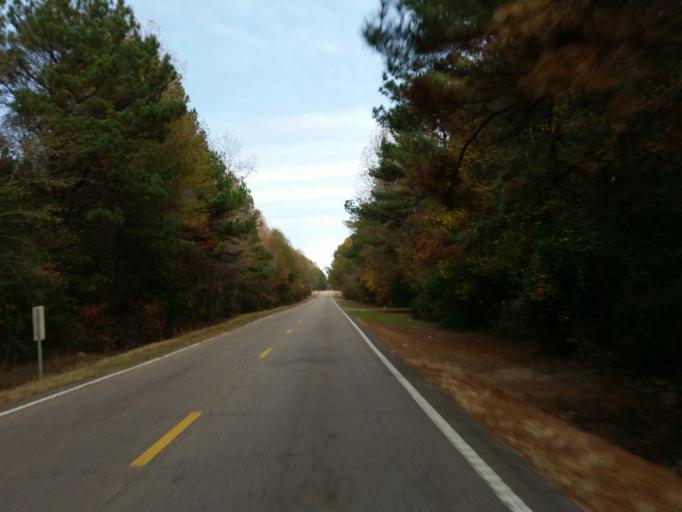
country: US
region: Mississippi
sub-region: Lauderdale County
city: Marion
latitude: 32.4191
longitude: -88.4947
